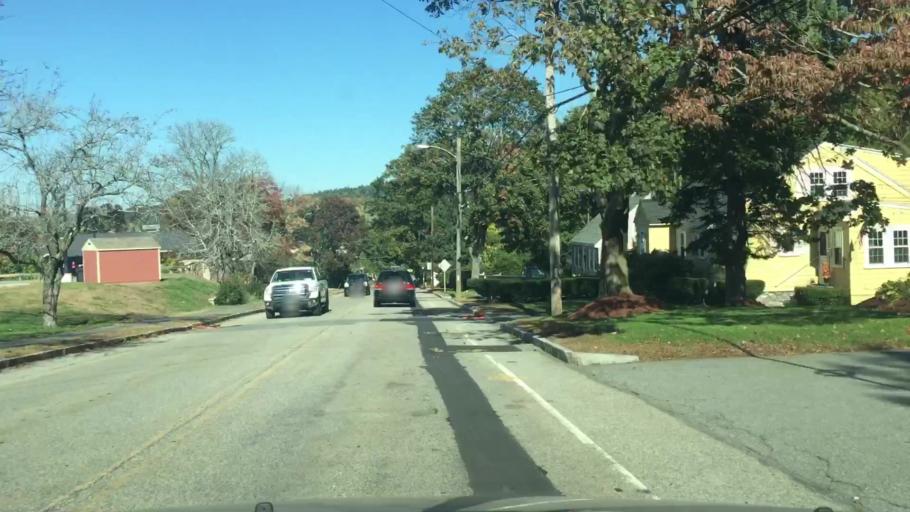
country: US
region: Massachusetts
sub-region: Essex County
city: North Andover
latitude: 42.6909
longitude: -71.1180
